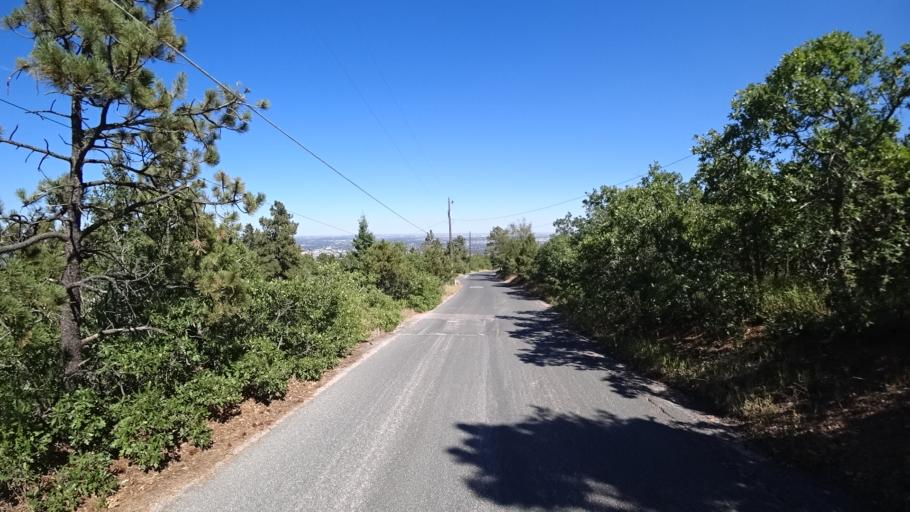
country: US
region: Colorado
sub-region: El Paso County
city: Manitou Springs
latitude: 38.8129
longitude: -104.8786
